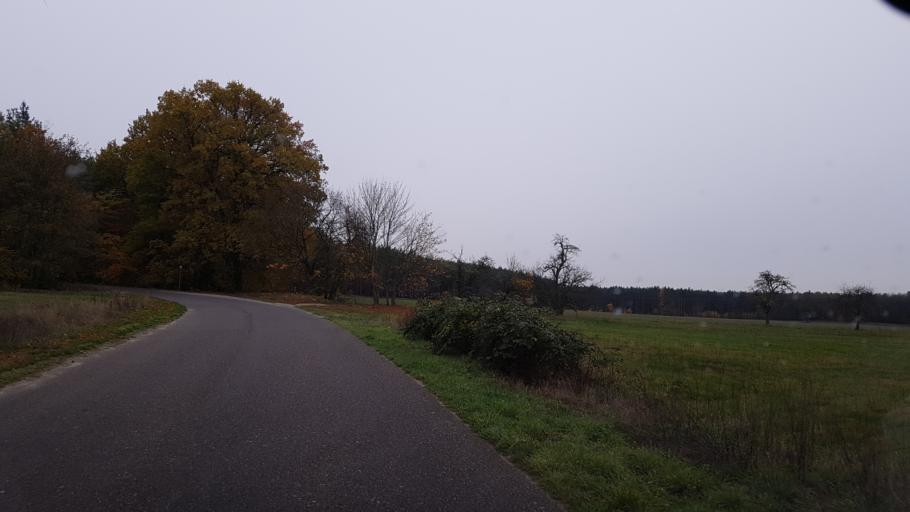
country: DE
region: Brandenburg
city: Crinitz
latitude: 51.7297
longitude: 13.7631
